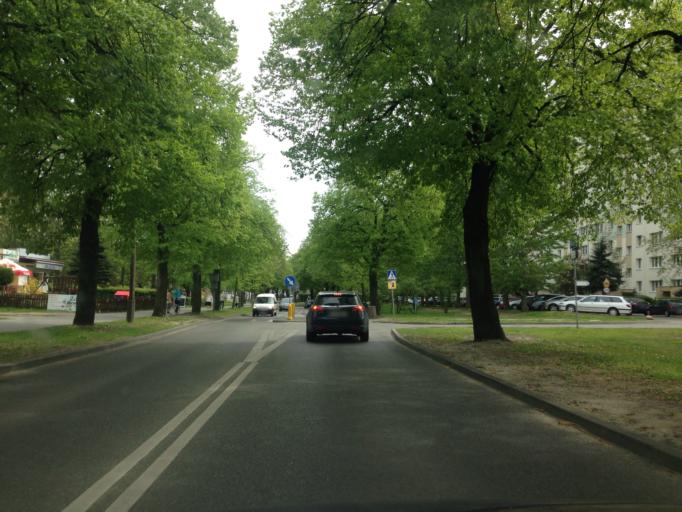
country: PL
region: Pomeranian Voivodeship
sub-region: Sopot
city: Sopot
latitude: 54.4226
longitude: 18.5797
